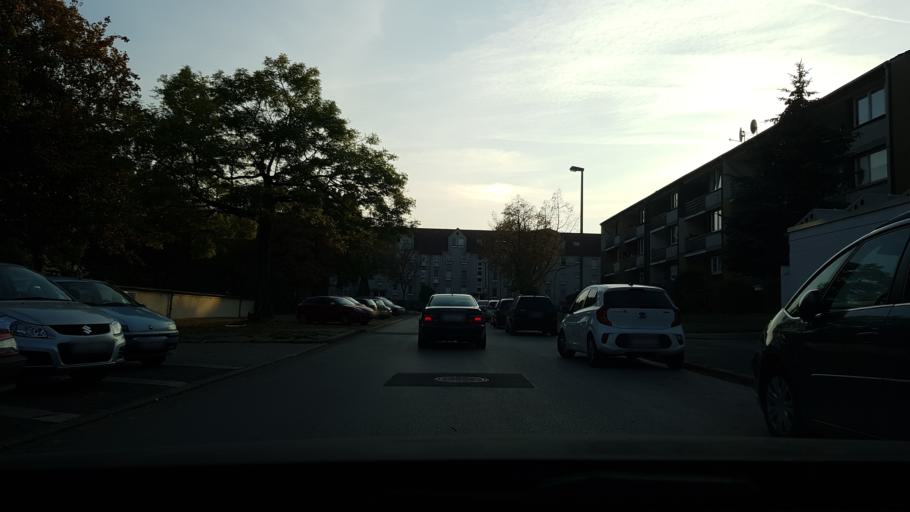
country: DE
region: North Rhine-Westphalia
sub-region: Regierungsbezirk Dusseldorf
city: Hochfeld
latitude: 51.3998
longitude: 6.7034
